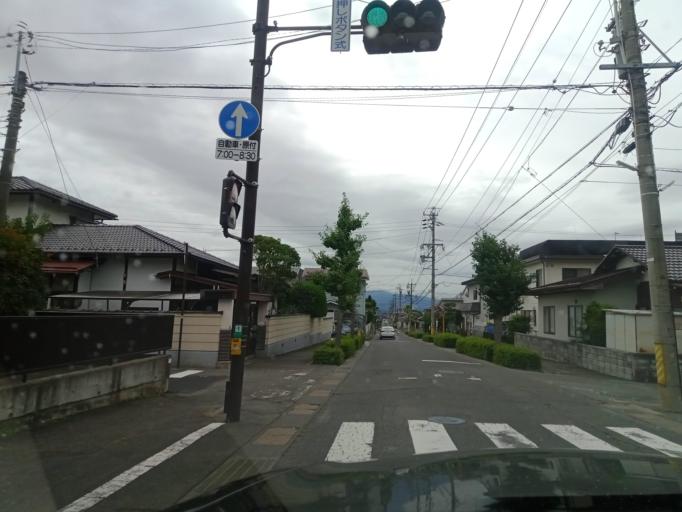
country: JP
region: Nagano
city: Nagano-shi
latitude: 36.6829
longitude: 138.2079
